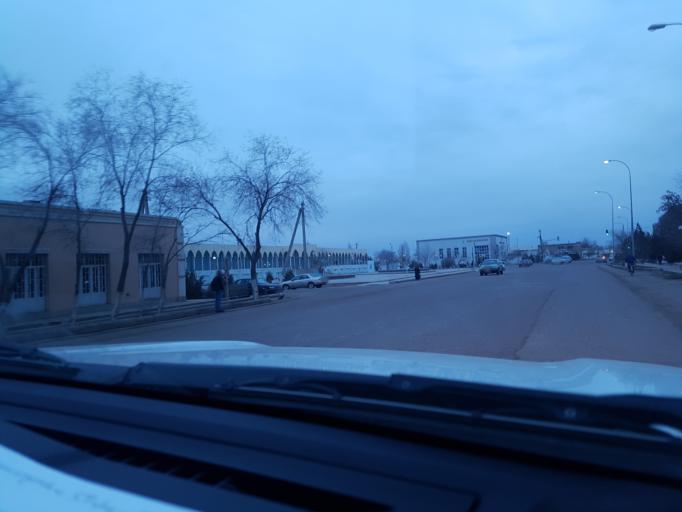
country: TM
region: Dasoguz
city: Yylanly
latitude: 41.8783
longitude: 59.6320
